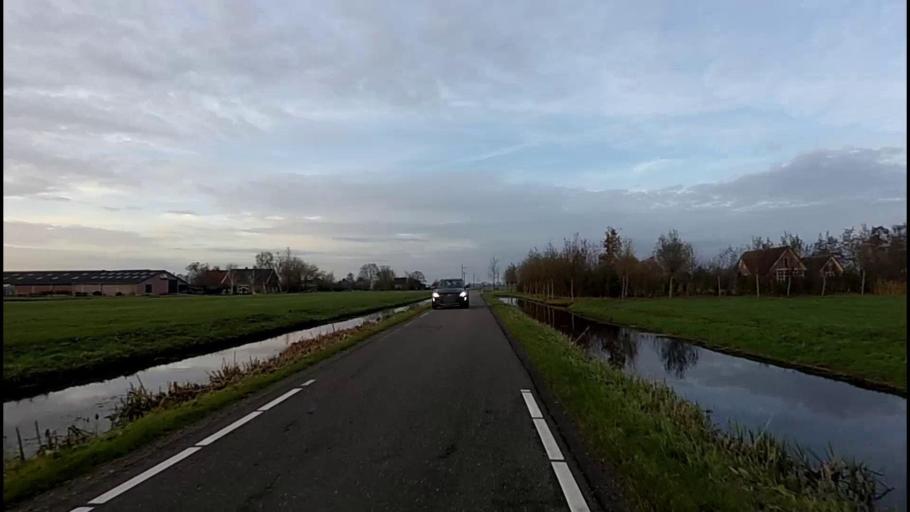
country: NL
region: South Holland
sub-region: Gemeente Vlist
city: Haastrecht
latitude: 51.9819
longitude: 4.7644
